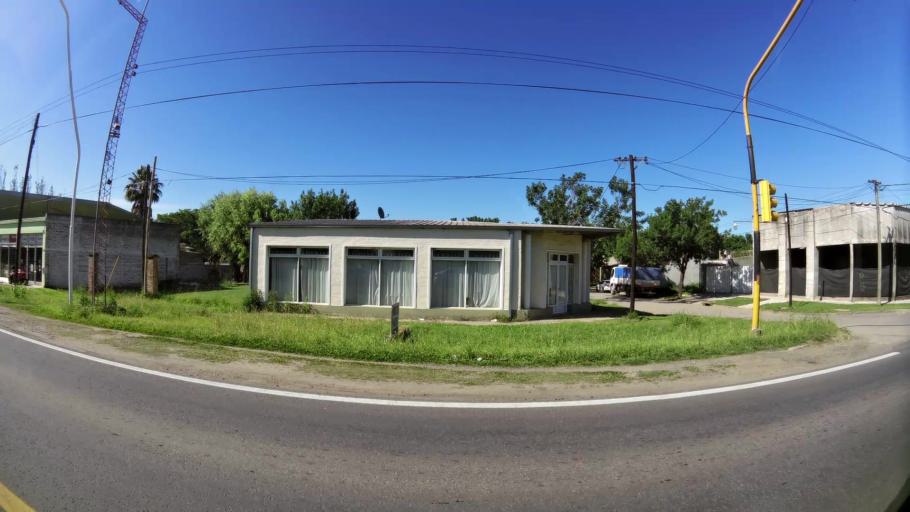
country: AR
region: Santa Fe
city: Esperanza
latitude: -31.4487
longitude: -60.9045
